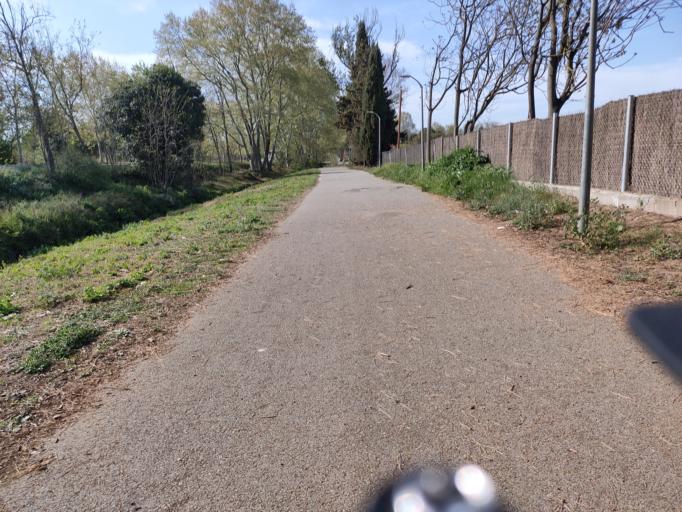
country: ES
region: Catalonia
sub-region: Provincia de Barcelona
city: Mollet del Valles
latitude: 41.5523
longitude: 2.2228
